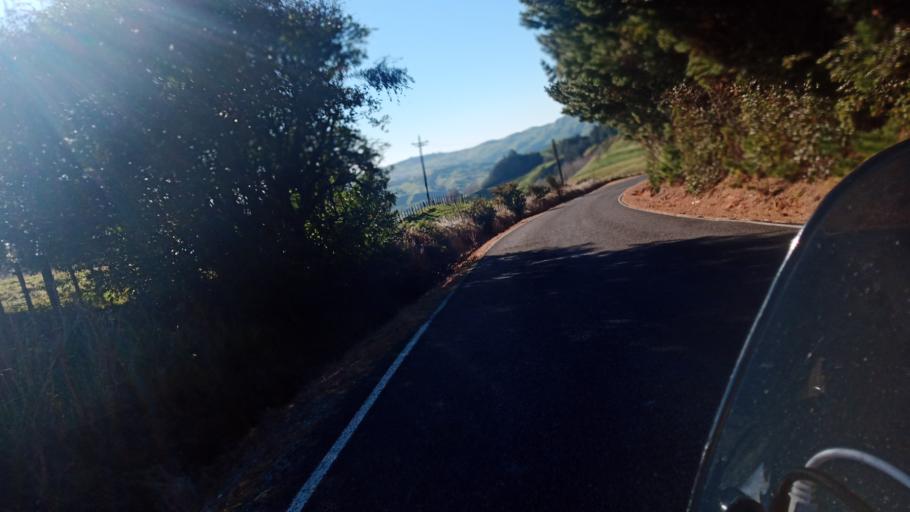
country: NZ
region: Hawke's Bay
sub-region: Wairoa District
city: Wairoa
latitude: -38.8324
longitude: 177.2732
